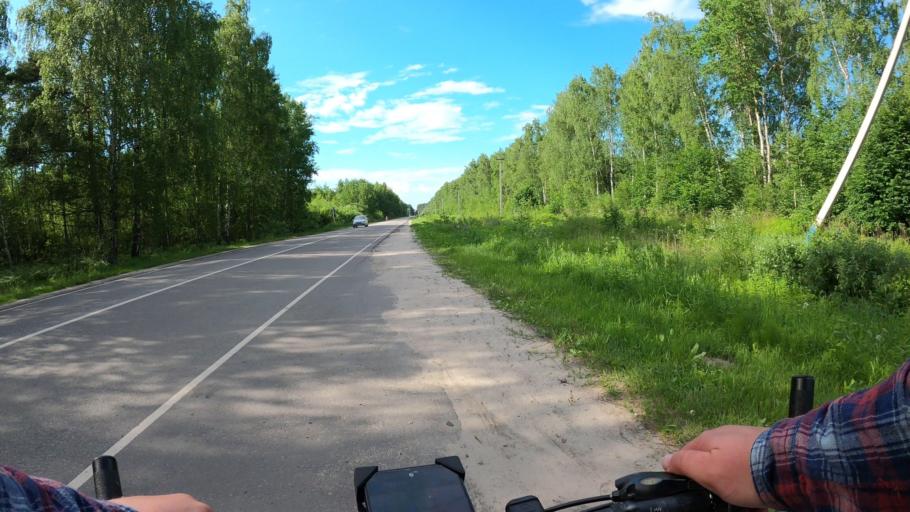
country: RU
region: Moskovskaya
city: Konobeyevo
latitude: 55.4273
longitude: 38.6626
